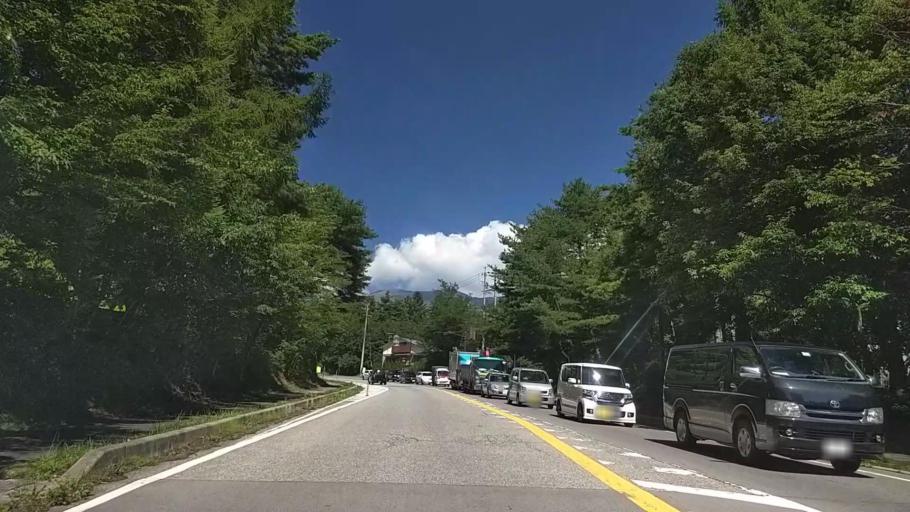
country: JP
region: Nagano
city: Komoro
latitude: 36.3370
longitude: 138.5363
